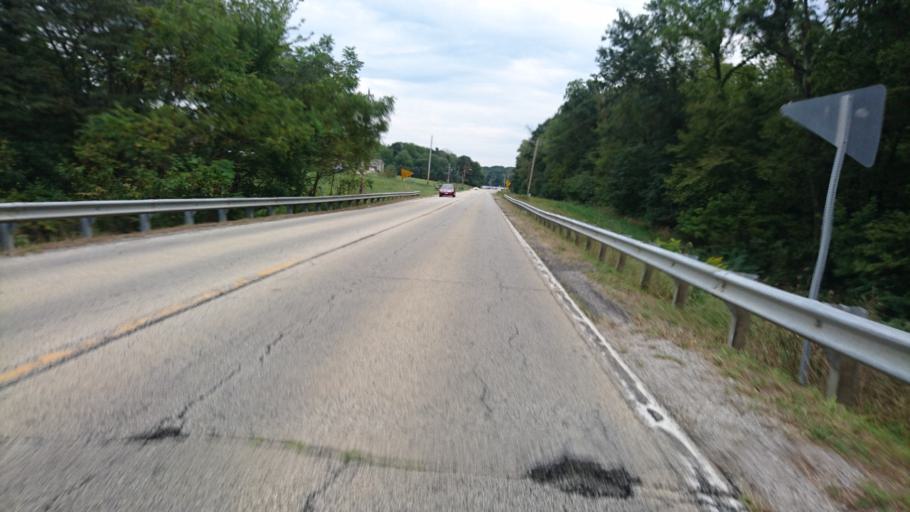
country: US
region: Illinois
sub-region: Sangamon County
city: Chatham
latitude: 39.6768
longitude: -89.6723
